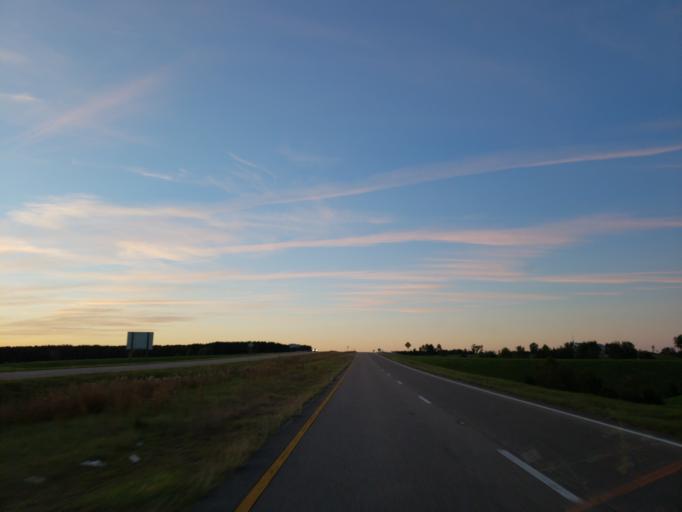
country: US
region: Mississippi
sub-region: Wayne County
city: Waynesboro
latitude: 31.7050
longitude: -88.6241
